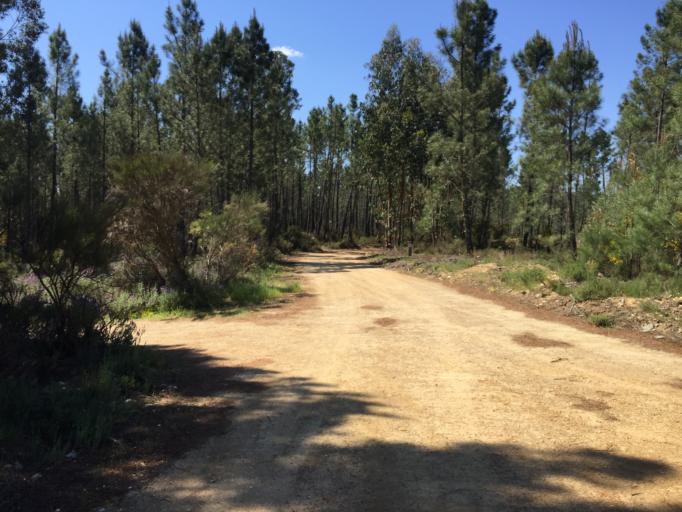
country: PT
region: Coimbra
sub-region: Pampilhosa da Serra
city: Pampilhosa da Serra
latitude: 40.0790
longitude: -7.7785
